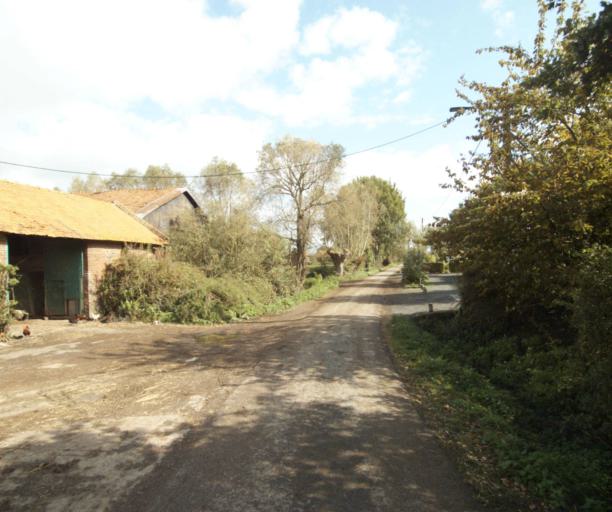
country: FR
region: Nord-Pas-de-Calais
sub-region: Departement du Nord
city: Deulemont
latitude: 50.7105
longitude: 2.9679
